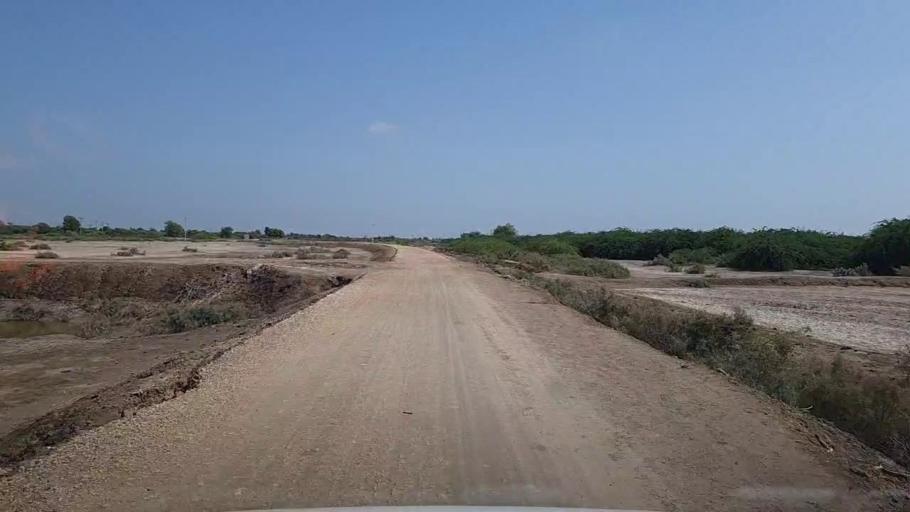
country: PK
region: Sindh
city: Talhar
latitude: 24.8357
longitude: 68.7176
